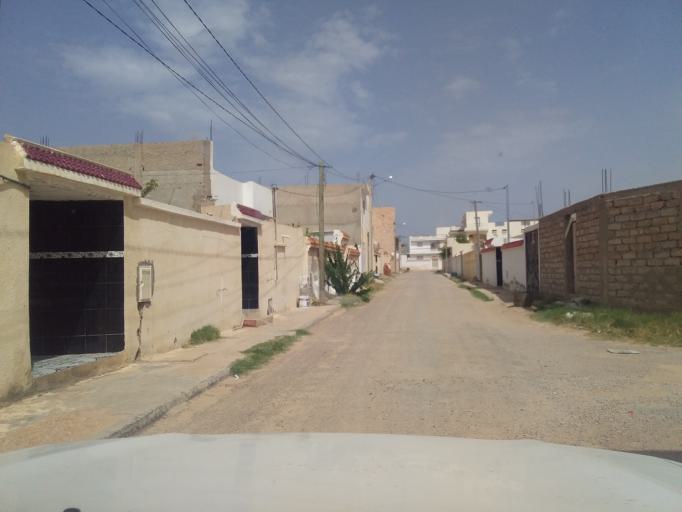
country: TN
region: Qabis
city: Matmata
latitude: 33.6163
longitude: 10.2788
